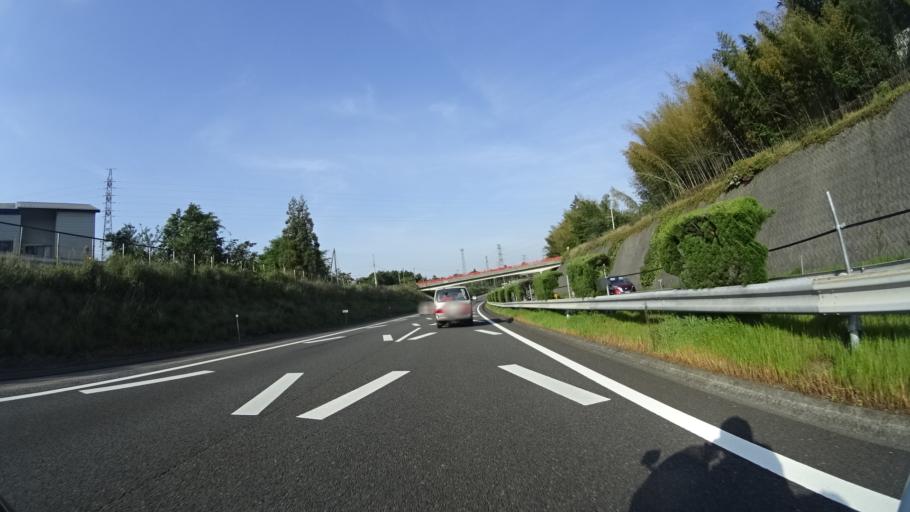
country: JP
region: Ehime
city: Niihama
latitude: 33.9391
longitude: 133.3827
